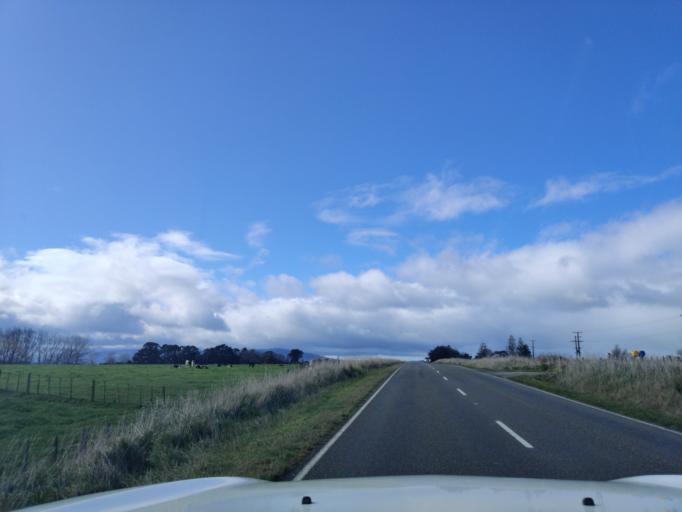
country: NZ
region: Manawatu-Wanganui
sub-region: Palmerston North City
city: Palmerston North
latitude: -40.2880
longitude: 175.6800
